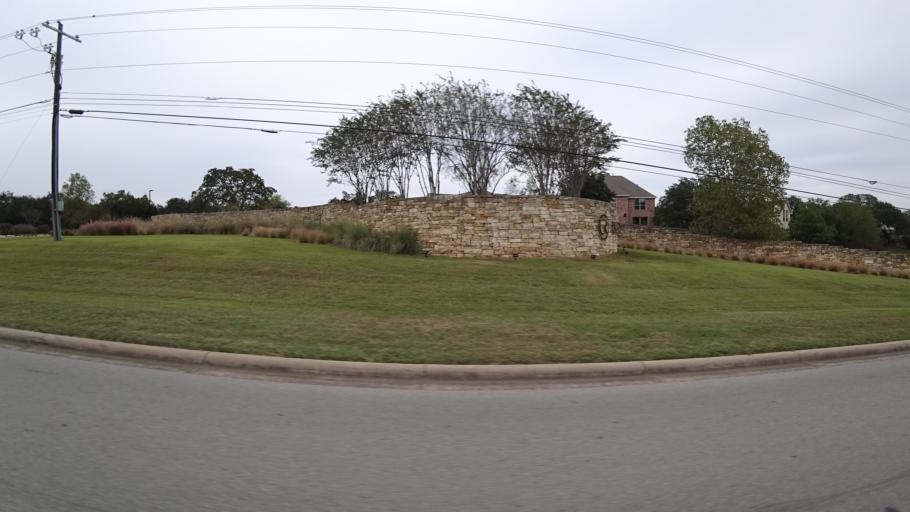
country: US
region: Texas
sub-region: Travis County
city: Shady Hollow
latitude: 30.1841
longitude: -97.9050
